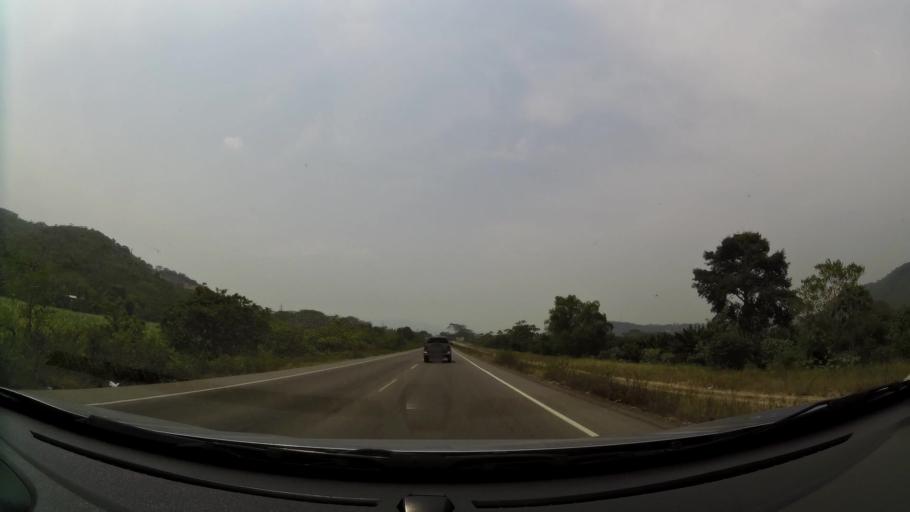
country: HN
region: Cortes
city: Potrerillos
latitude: 15.2579
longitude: -87.9583
